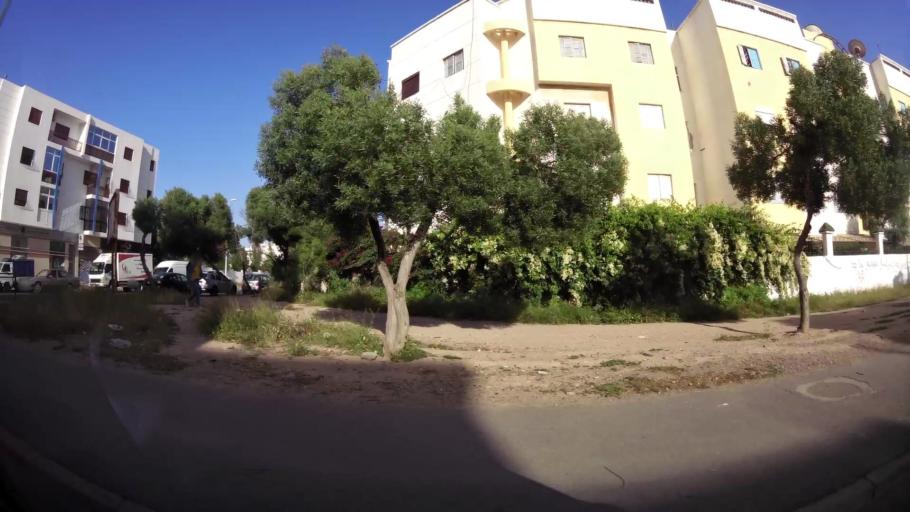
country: MA
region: Oued ed Dahab-Lagouira
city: Dakhla
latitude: 30.3975
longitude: -9.5446
